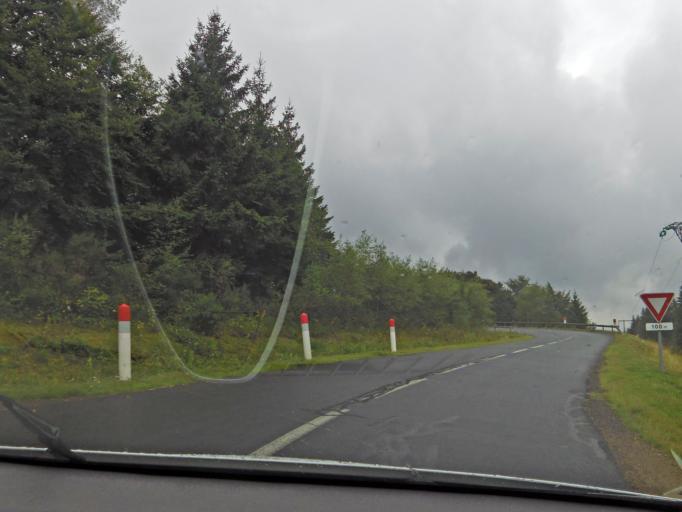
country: FR
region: Auvergne
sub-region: Departement du Puy-de-Dome
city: Saint-Genes-Champanelle
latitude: 45.7415
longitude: 2.9466
